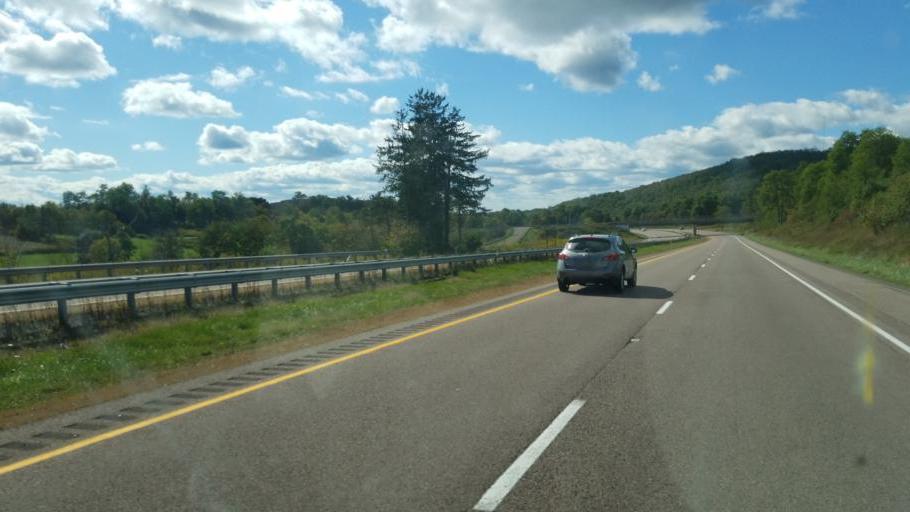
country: US
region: Pennsylvania
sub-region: Somerset County
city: Meyersdale
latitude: 39.7014
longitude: -79.3027
